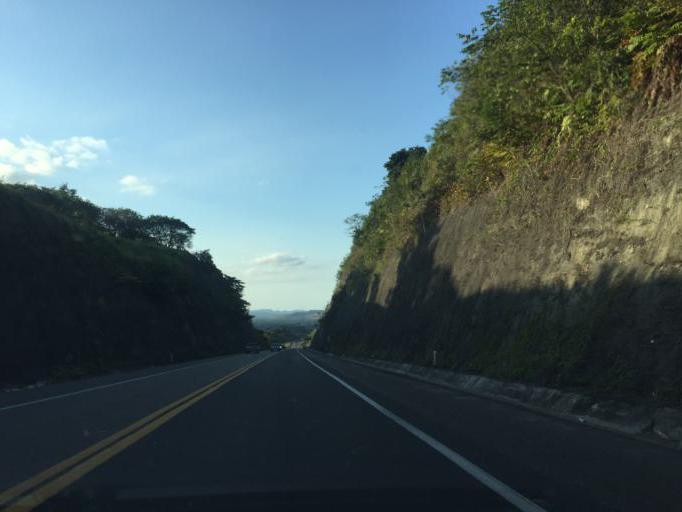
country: MX
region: Veracruz
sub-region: Papantla
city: Residencial Tajin
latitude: 20.6027
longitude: -97.3809
